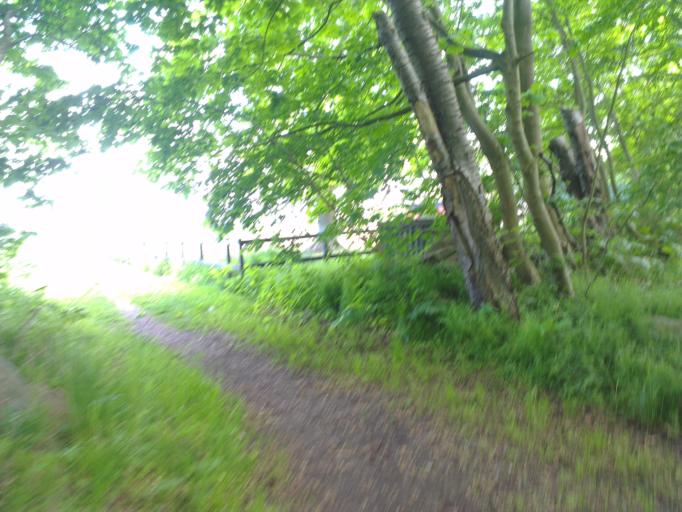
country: DK
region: Capital Region
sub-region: Frederikssund Kommune
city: Jaegerspris
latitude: 55.8686
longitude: 11.9889
